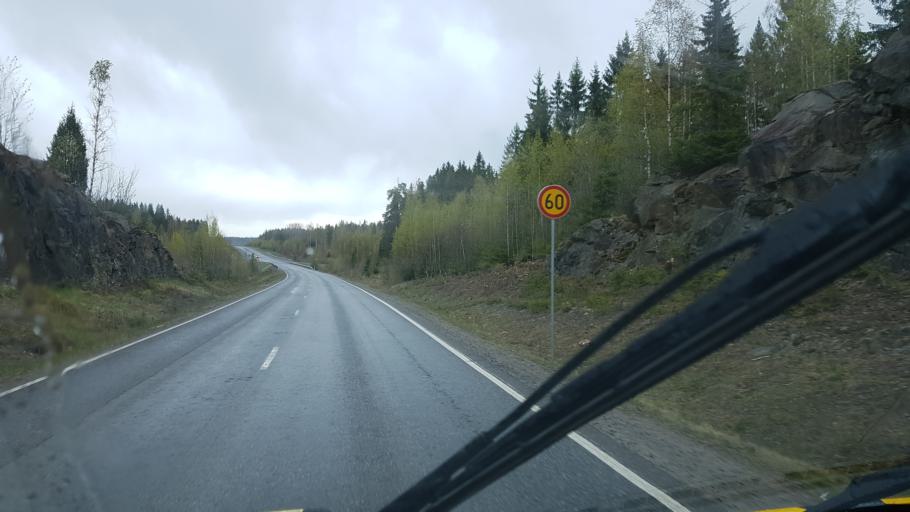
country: FI
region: Pirkanmaa
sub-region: Tampere
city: Pirkkala
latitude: 61.4068
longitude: 23.6333
